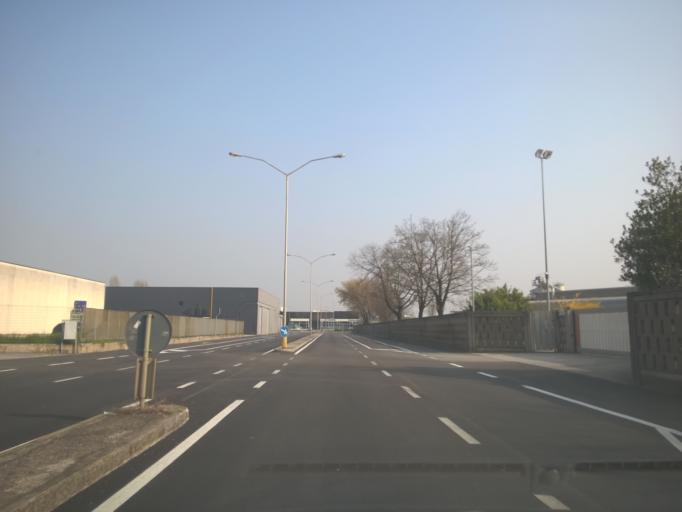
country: IT
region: Veneto
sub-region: Provincia di Vicenza
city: Creazzo
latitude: 45.5243
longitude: 11.5101
